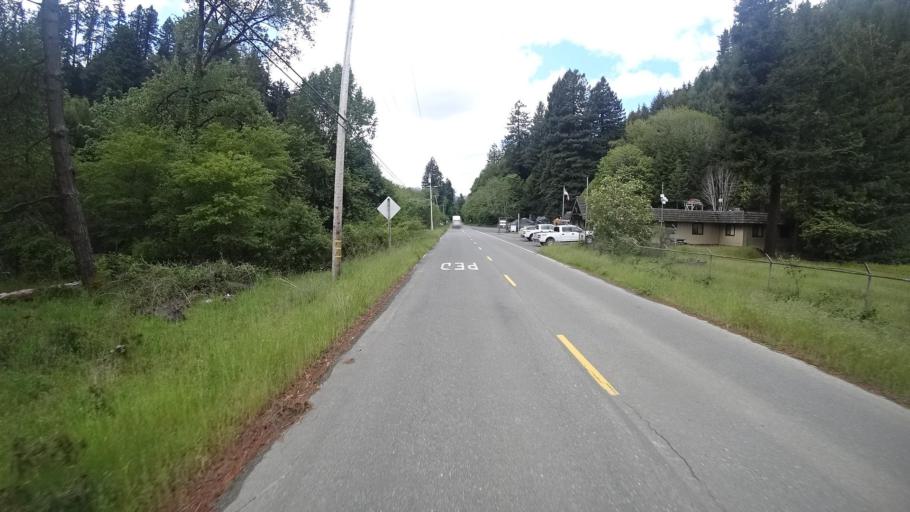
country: US
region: California
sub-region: Humboldt County
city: Blue Lake
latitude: 40.8696
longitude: -123.9643
